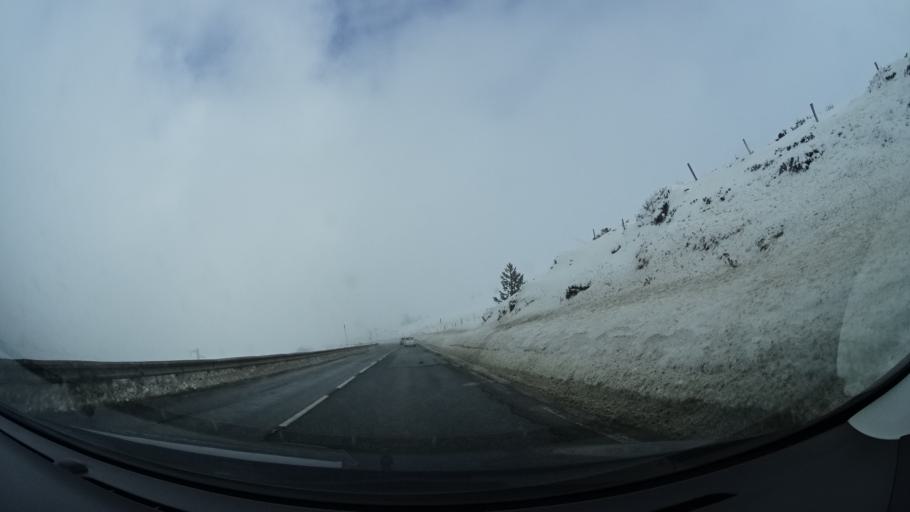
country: AD
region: Encamp
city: Pas de la Casa
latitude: 42.5540
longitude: 1.7412
